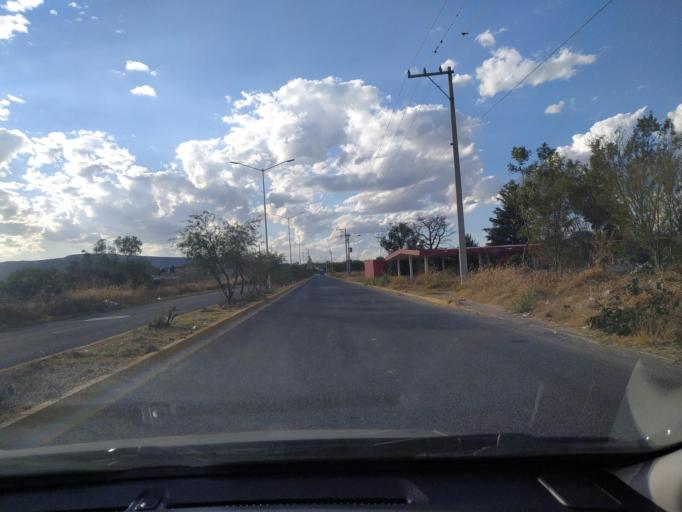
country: LA
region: Oudomxai
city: Muang La
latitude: 21.0172
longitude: 101.8321
